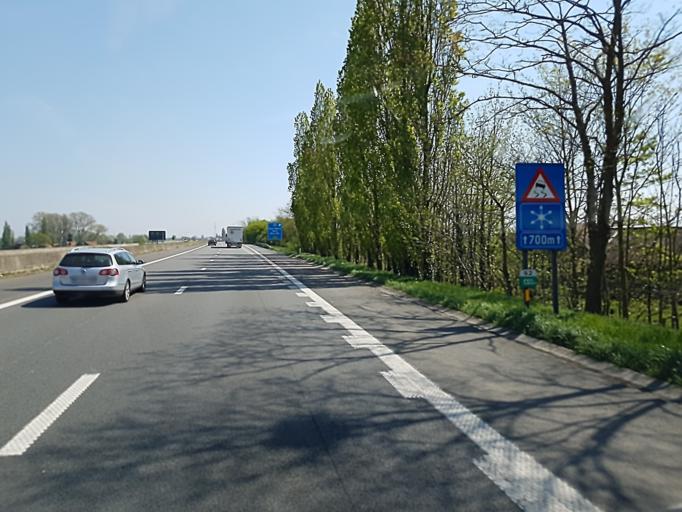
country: BE
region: Flanders
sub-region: Provincie West-Vlaanderen
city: Menen
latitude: 50.8180
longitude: 3.0887
